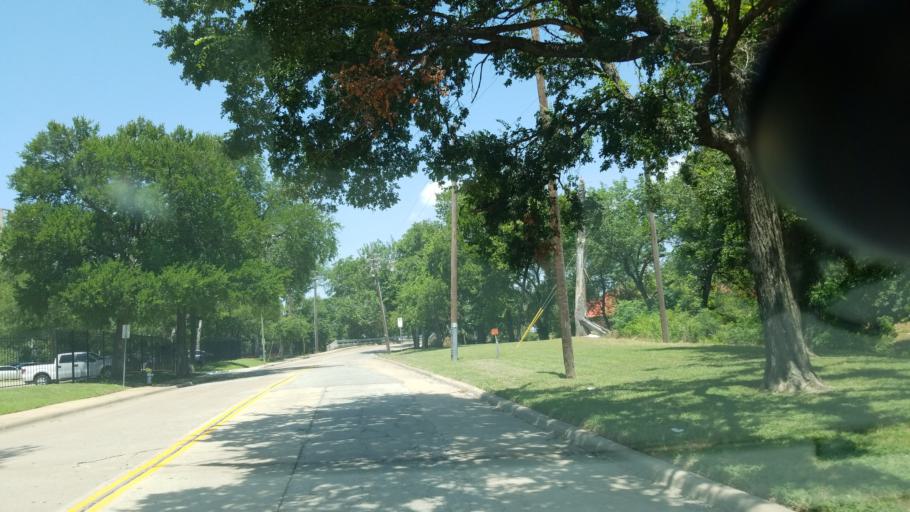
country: US
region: Texas
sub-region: Dallas County
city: Dallas
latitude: 32.8179
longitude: -96.8637
